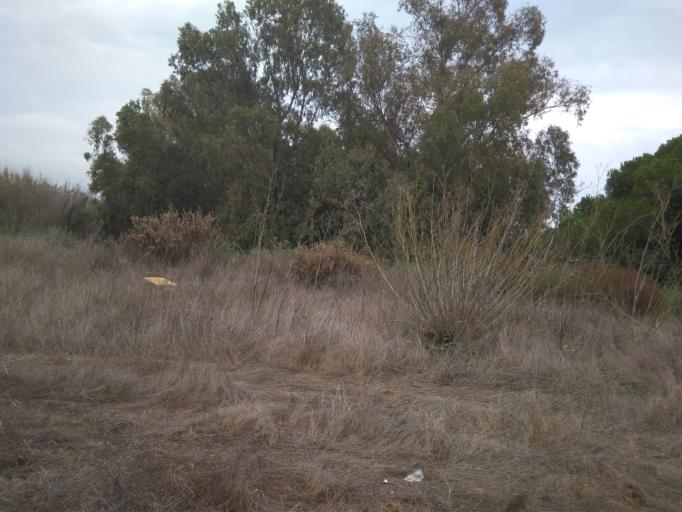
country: PT
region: Faro
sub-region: Loule
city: Almancil
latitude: 37.0252
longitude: -8.0061
